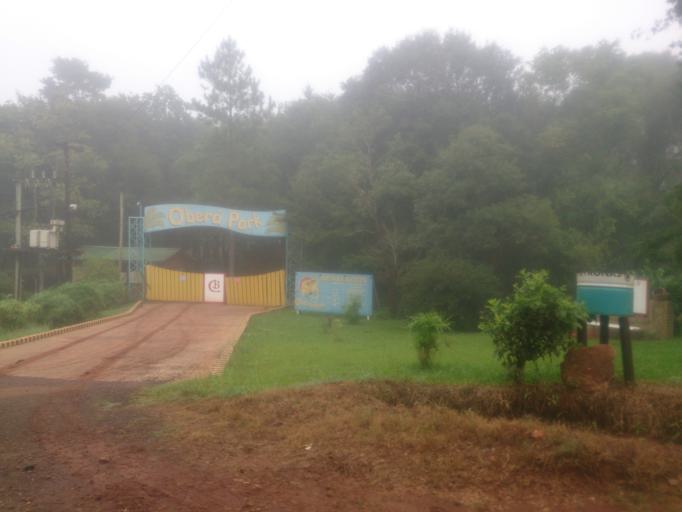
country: AR
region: Misiones
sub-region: Departamento de Obera
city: Obera
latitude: -27.4630
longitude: -55.1061
